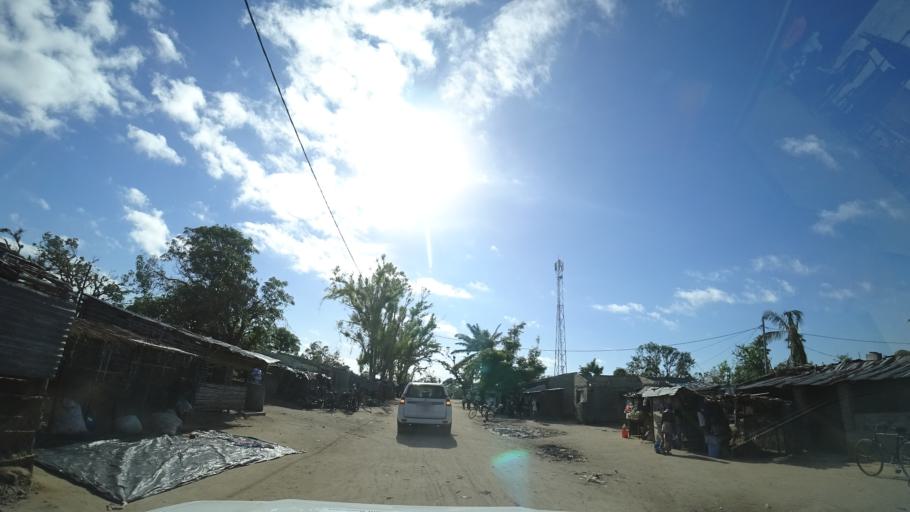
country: MZ
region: Sofala
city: Beira
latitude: -19.7164
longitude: 35.0069
